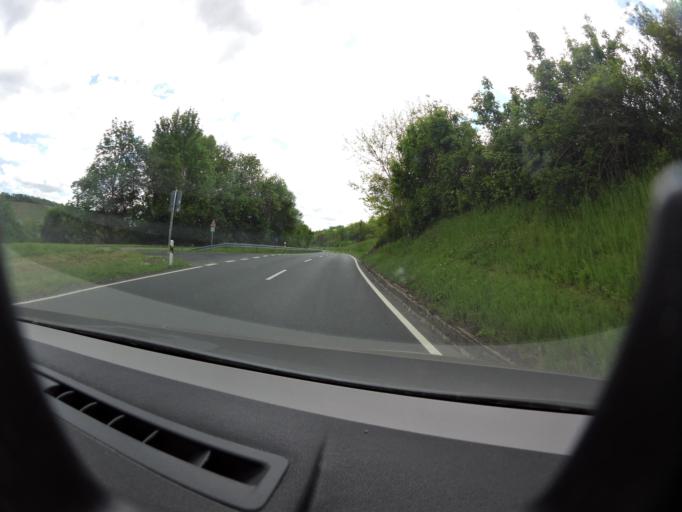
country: DE
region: Bavaria
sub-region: Regierungsbezirk Unterfranken
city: Sommerhausen
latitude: 49.6935
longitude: 10.0200
